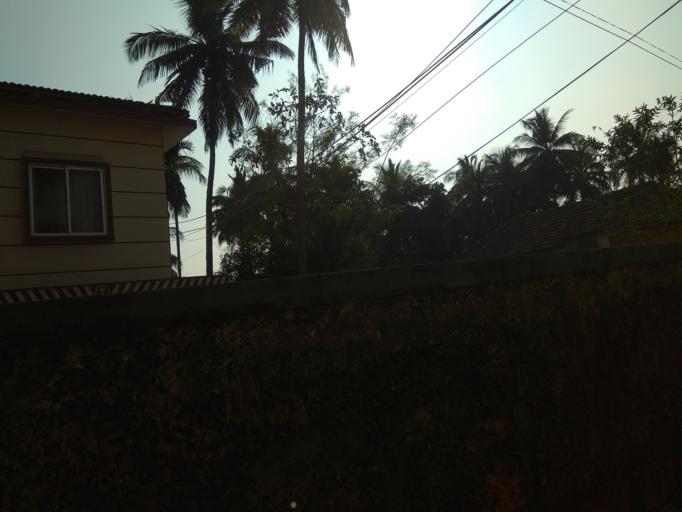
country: IN
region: Karnataka
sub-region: Dakshina Kannada
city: Mangalore
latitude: 12.9233
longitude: 74.8698
